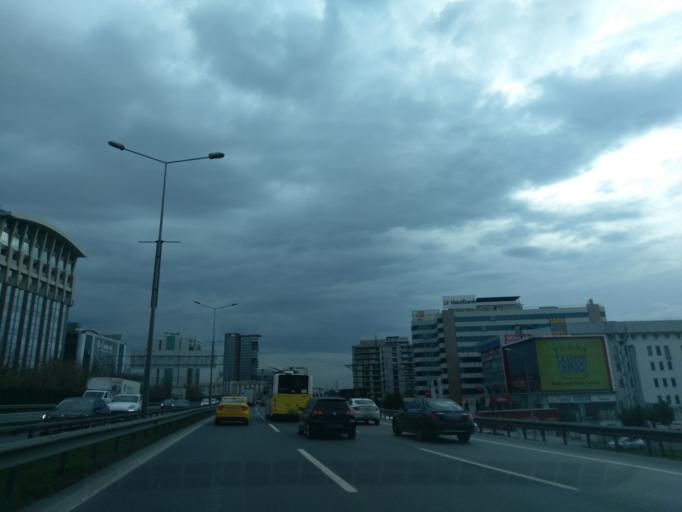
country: TR
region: Istanbul
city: Mahmutbey
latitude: 41.0399
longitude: 28.8099
